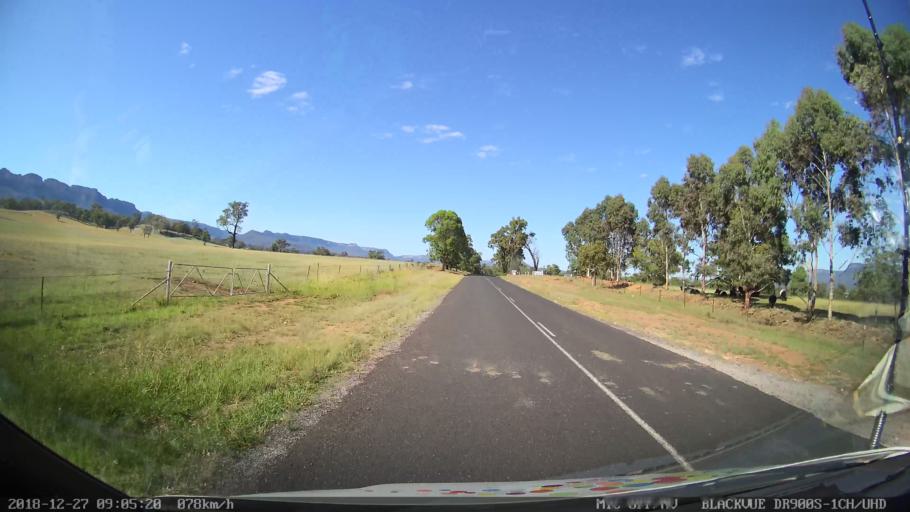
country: AU
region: New South Wales
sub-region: Lithgow
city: Portland
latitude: -33.1164
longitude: 150.1811
